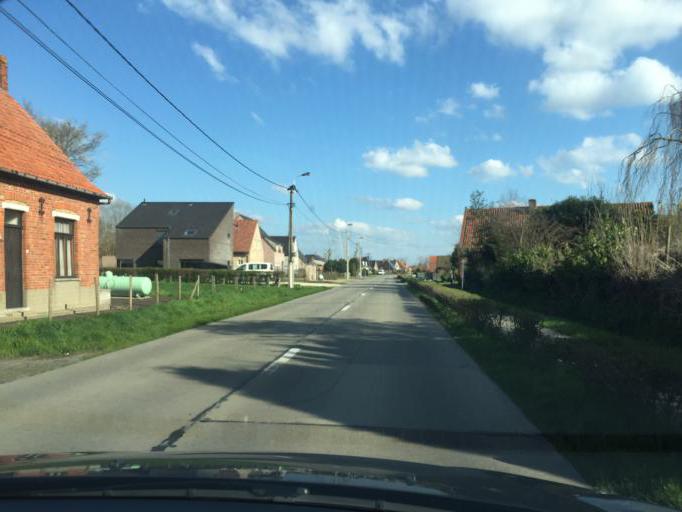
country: BE
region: Flanders
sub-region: Provincie West-Vlaanderen
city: Beernem
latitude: 51.1556
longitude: 3.3244
